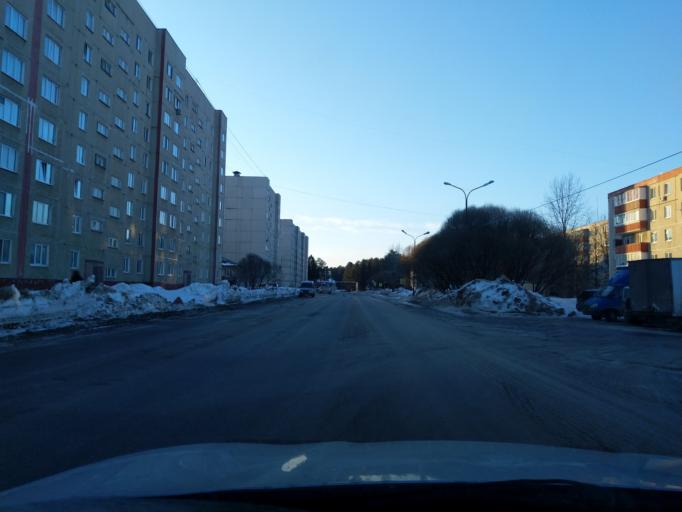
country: RU
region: Perm
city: Dobryanka
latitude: 58.4690
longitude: 56.3996
